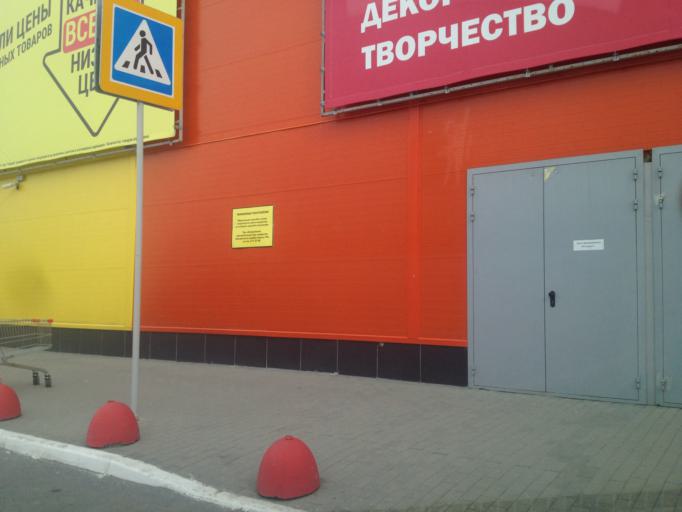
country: RU
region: Sverdlovsk
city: Shirokaya Rechka
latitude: 56.8165
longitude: 60.5348
